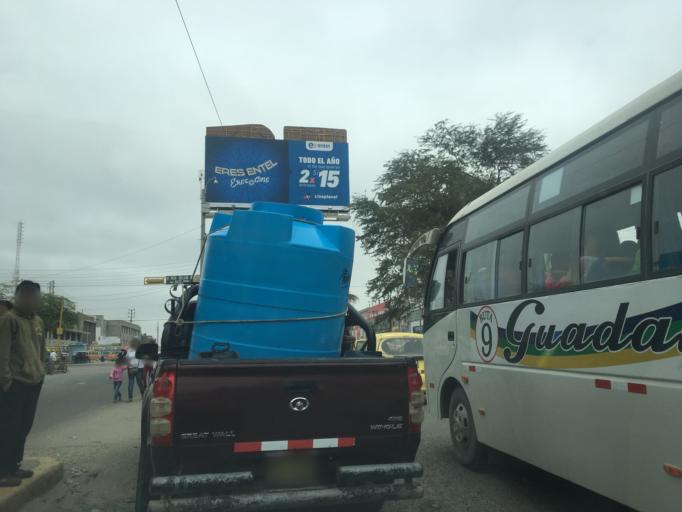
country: PE
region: Piura
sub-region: Provincia de Piura
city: Piura
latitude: -5.1897
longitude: -80.6349
